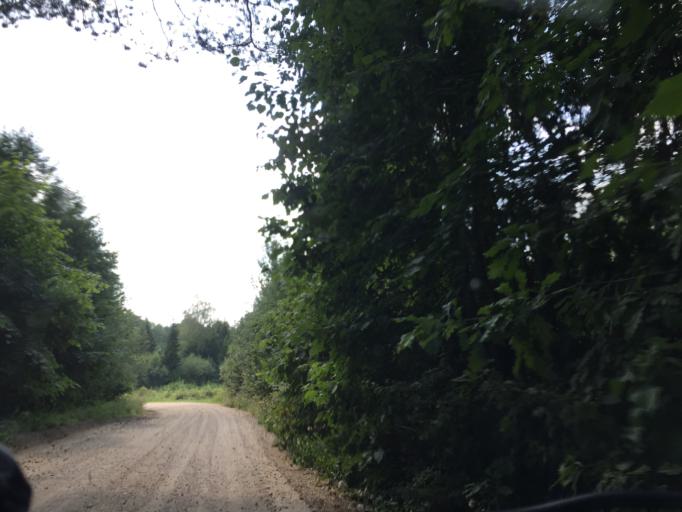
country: LT
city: Zagare
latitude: 56.3735
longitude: 23.1653
